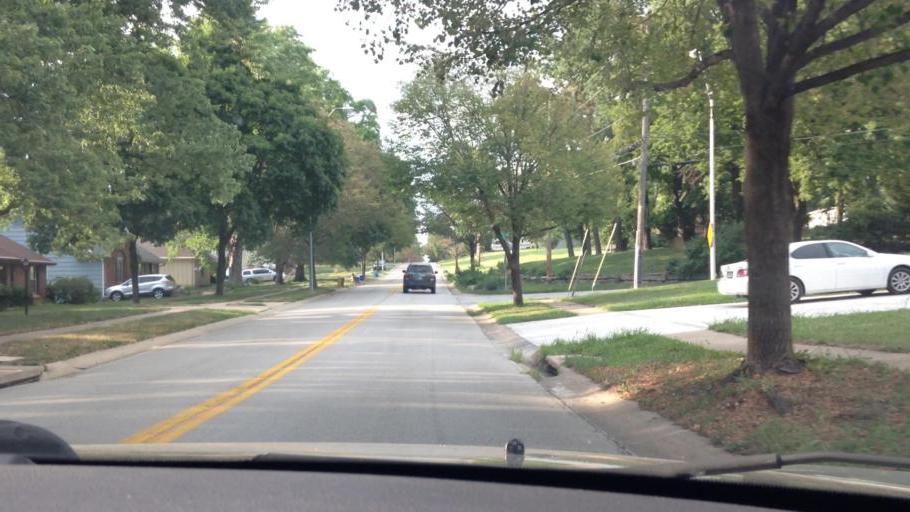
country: US
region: Missouri
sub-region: Platte County
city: Parkville
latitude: 39.2173
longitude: -94.6405
